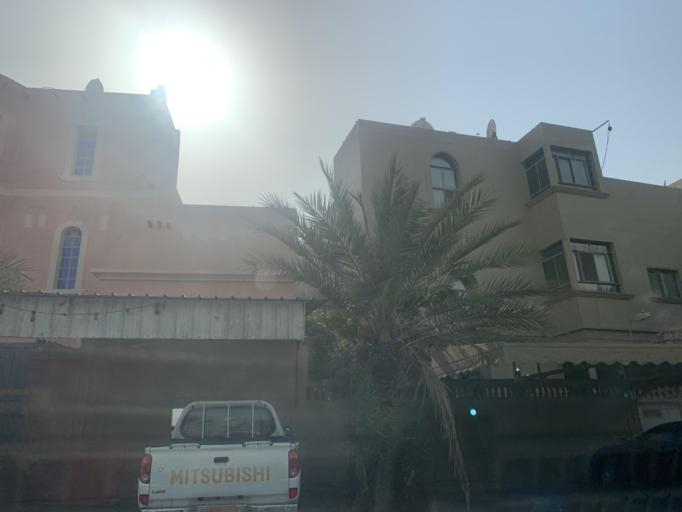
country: BH
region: Northern
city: Madinat `Isa
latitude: 26.1856
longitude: 50.4877
